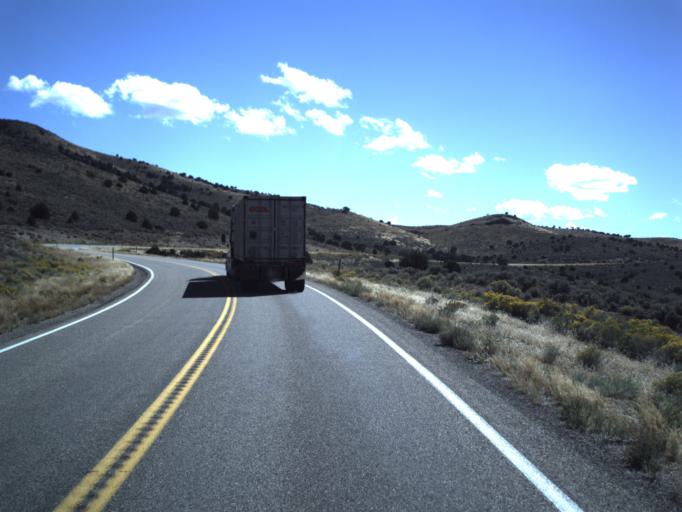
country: US
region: Utah
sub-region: Beaver County
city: Milford
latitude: 38.1128
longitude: -112.9510
